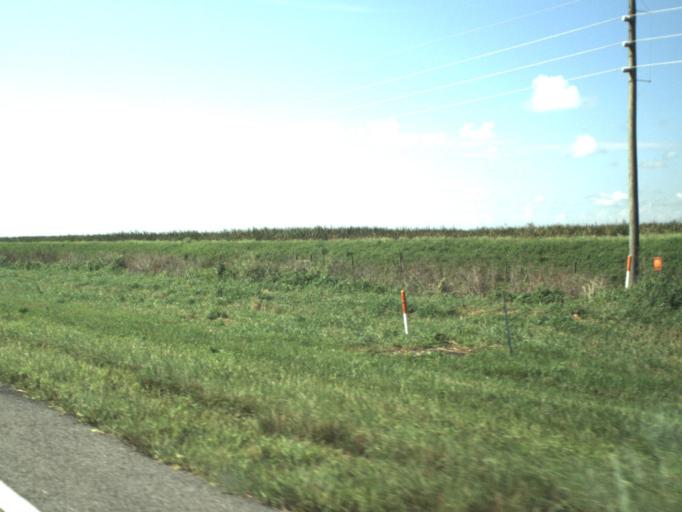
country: US
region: Florida
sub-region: Palm Beach County
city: Belle Glade Camp
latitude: 26.3785
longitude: -80.5717
